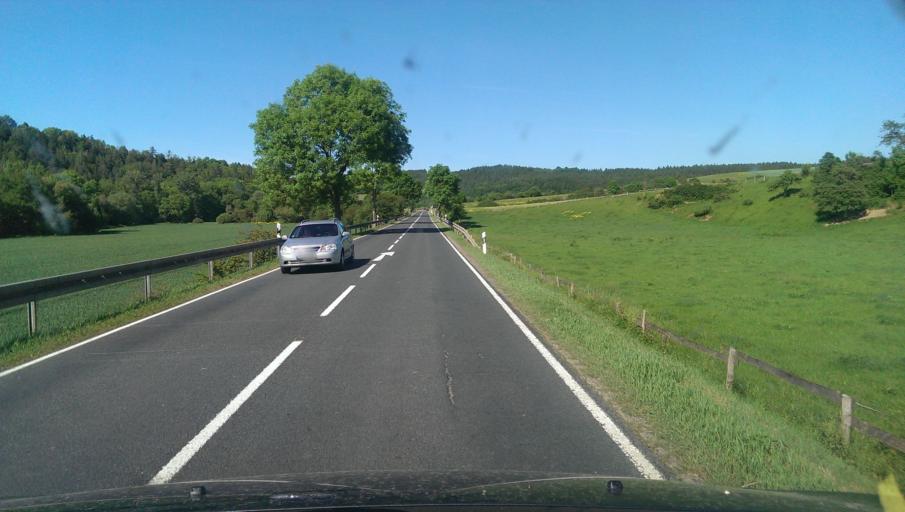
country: DE
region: Thuringia
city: Barchfeld
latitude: 50.8082
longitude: 11.1723
